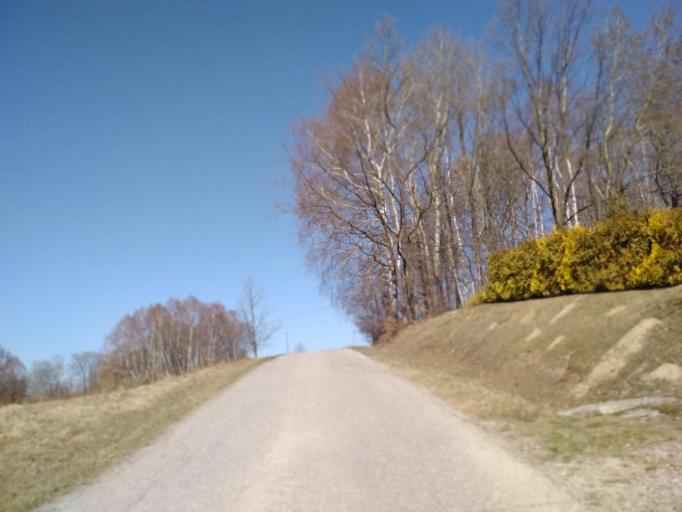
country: PL
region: Subcarpathian Voivodeship
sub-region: Powiat brzozowski
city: Jablonica Polska
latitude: 49.7365
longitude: 21.8955
